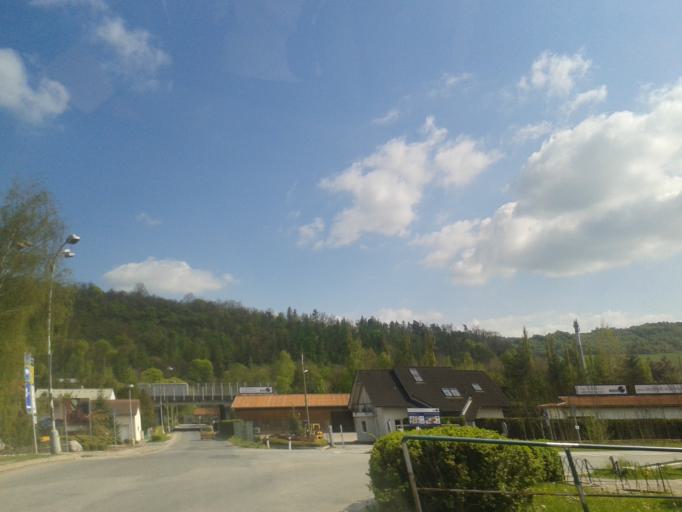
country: CZ
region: Central Bohemia
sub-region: Okres Beroun
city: Lodenice
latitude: 49.9943
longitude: 14.1585
